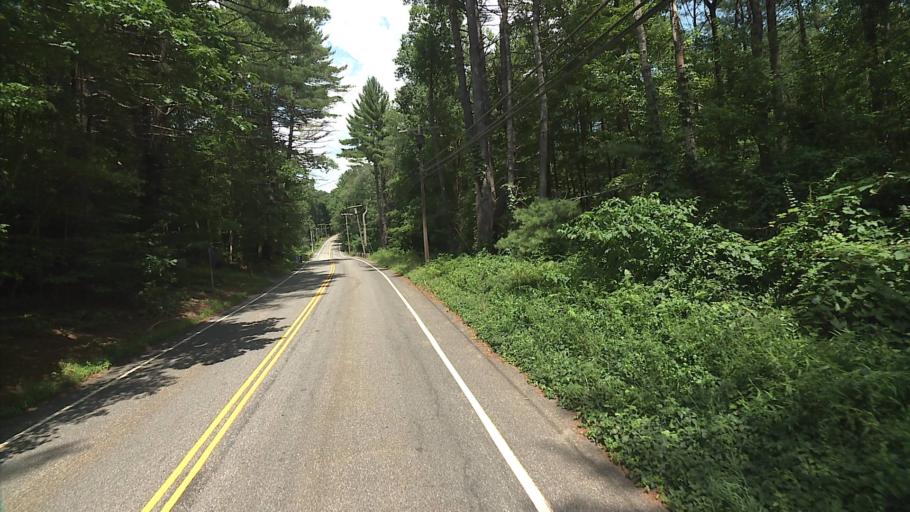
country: US
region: Connecticut
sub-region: Litchfield County
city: Winsted
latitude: 41.9758
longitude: -73.0171
